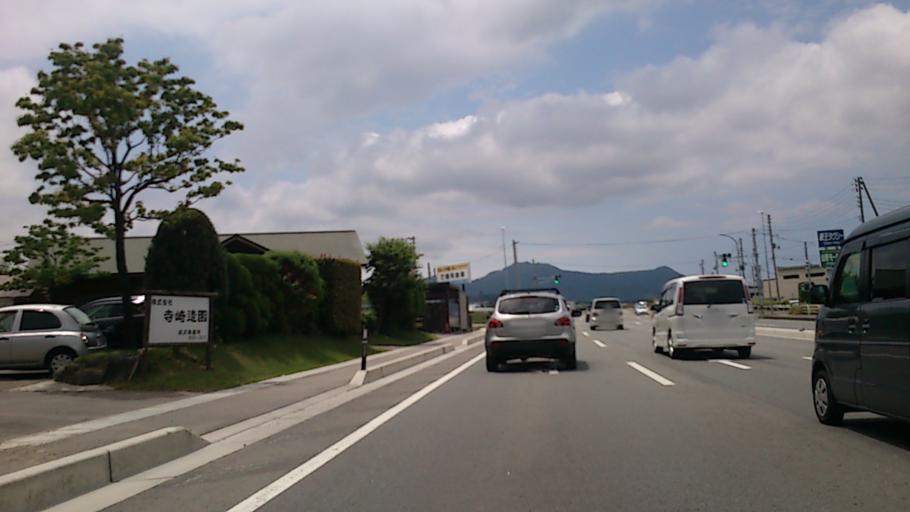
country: JP
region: Yamagata
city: Kaminoyama
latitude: 38.1996
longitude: 140.3148
